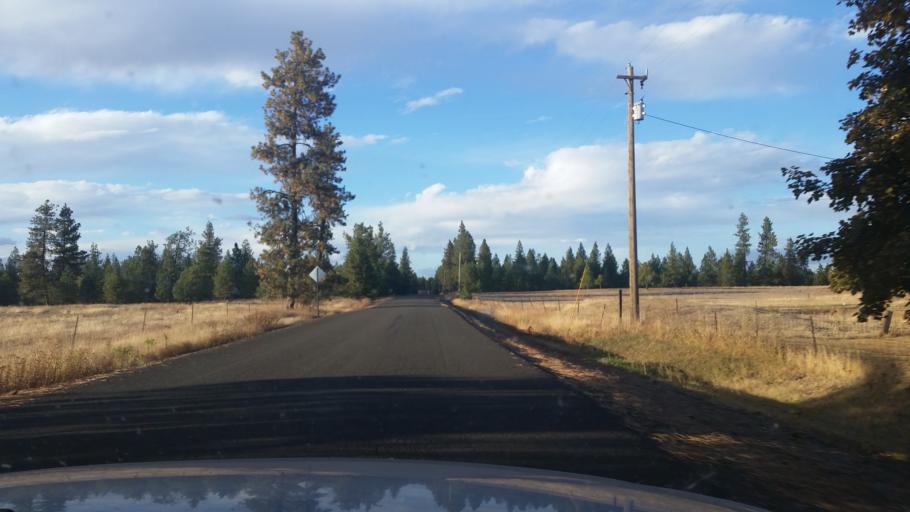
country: US
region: Washington
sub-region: Spokane County
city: Medical Lake
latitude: 47.4396
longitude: -117.7895
